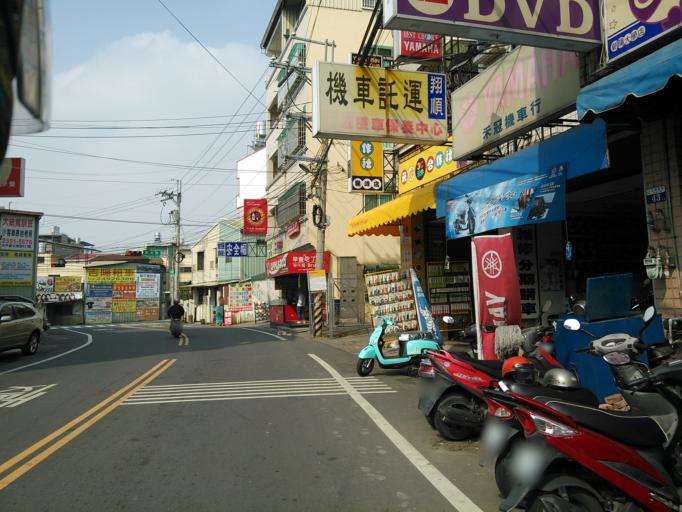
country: TW
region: Taiwan
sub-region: Taichung City
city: Taichung
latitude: 24.0753
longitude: 120.7145
